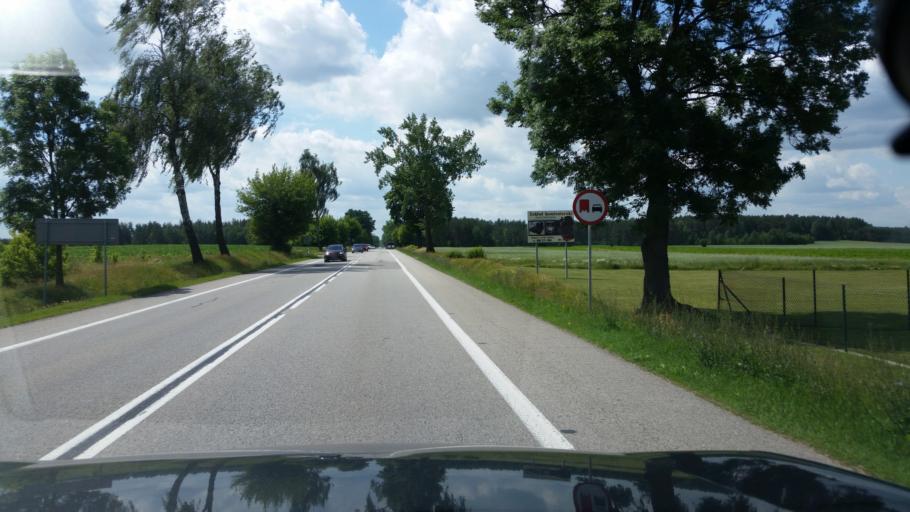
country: PL
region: Podlasie
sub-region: Powiat kolnenski
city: Stawiski
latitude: 53.2925
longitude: 22.1451
